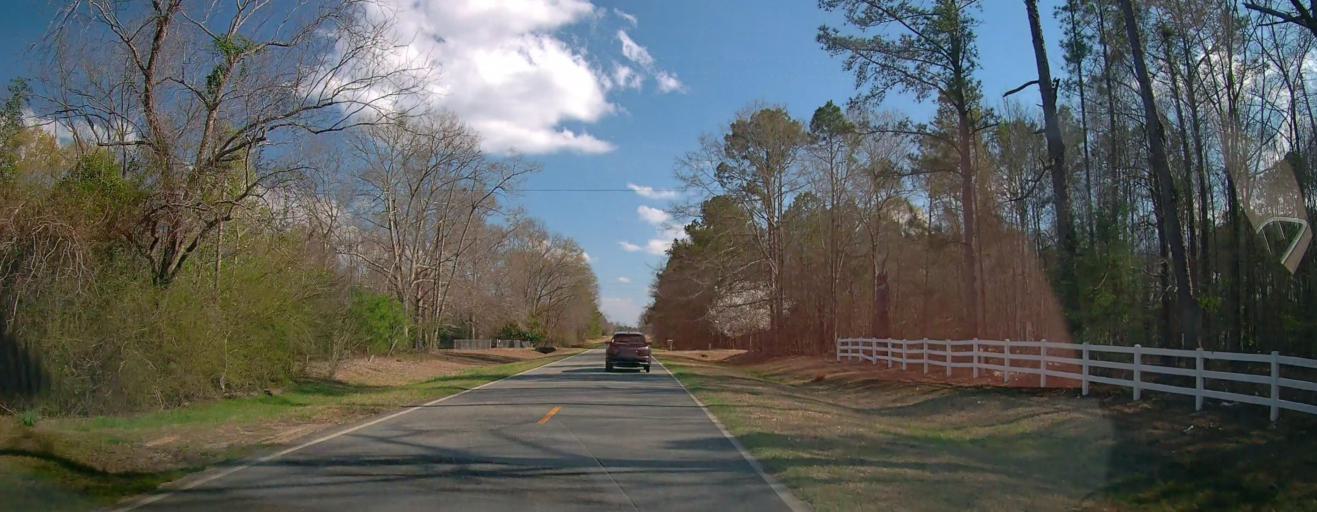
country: US
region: Georgia
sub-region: Laurens County
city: Dublin
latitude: 32.6108
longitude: -83.0806
